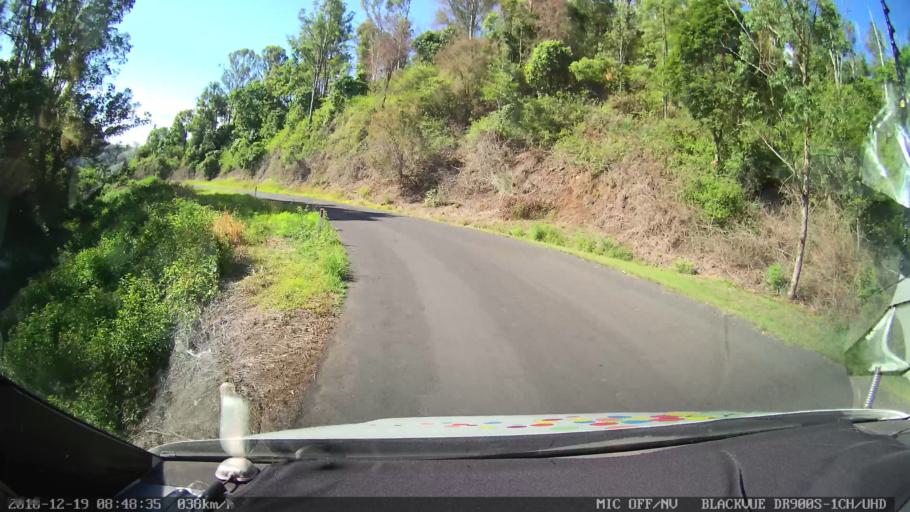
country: AU
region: New South Wales
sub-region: Kyogle
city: Kyogle
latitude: -28.3718
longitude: 152.9716
